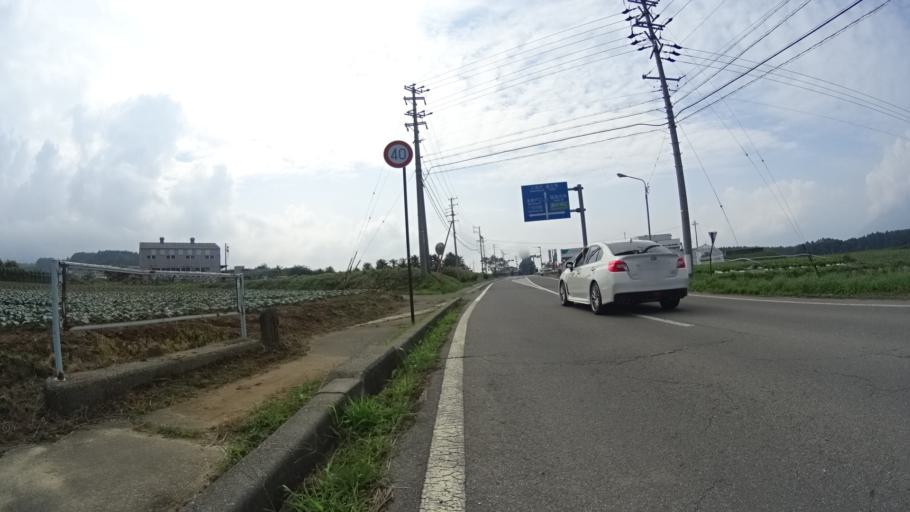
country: JP
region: Nagano
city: Chino
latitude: 35.9477
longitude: 138.2415
